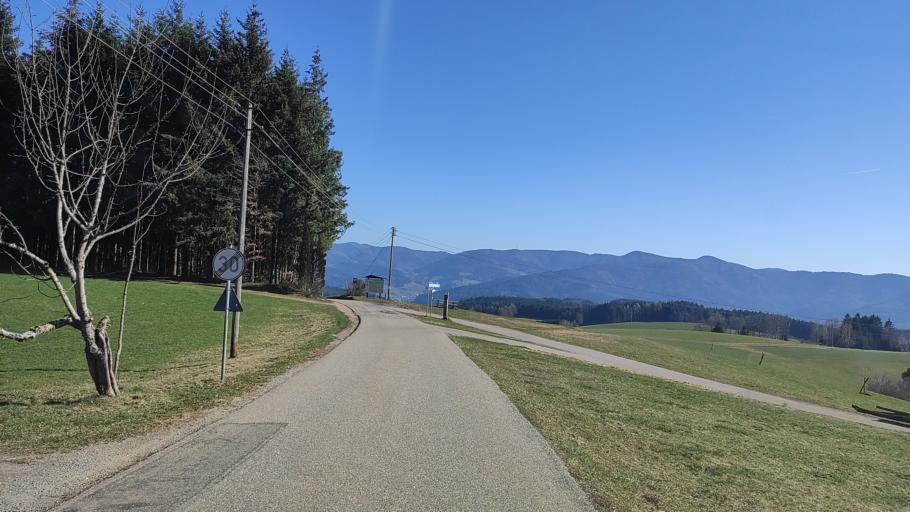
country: DE
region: Baden-Wuerttemberg
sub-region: Freiburg Region
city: Gutach im Breisgau
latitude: 48.1829
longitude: 8.0014
